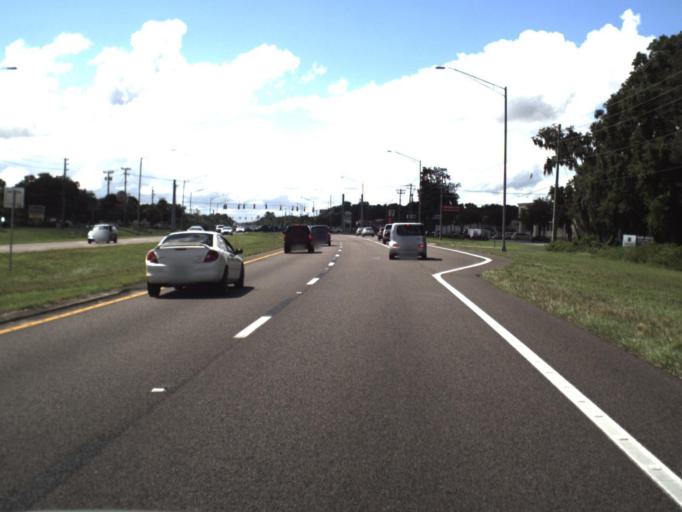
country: US
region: Florida
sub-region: Polk County
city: Medulla
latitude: 27.9411
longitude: -81.9741
